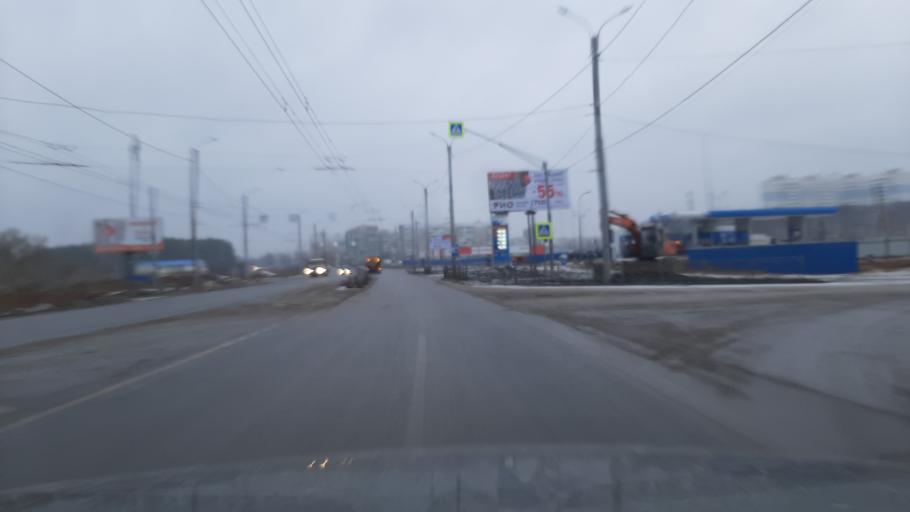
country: RU
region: Ivanovo
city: Kokhma
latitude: 56.9446
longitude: 41.0573
